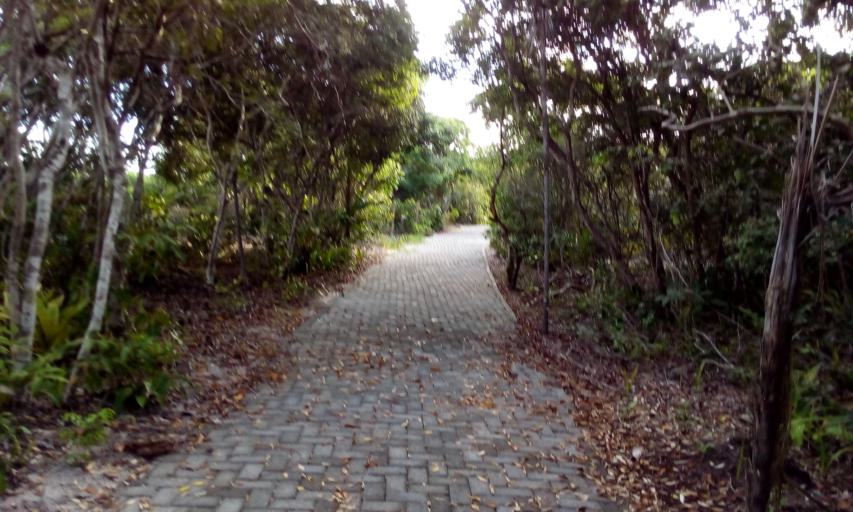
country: BR
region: Bahia
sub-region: Mata De Sao Joao
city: Mata de Sao Joao
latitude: -12.5640
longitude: -37.9993
